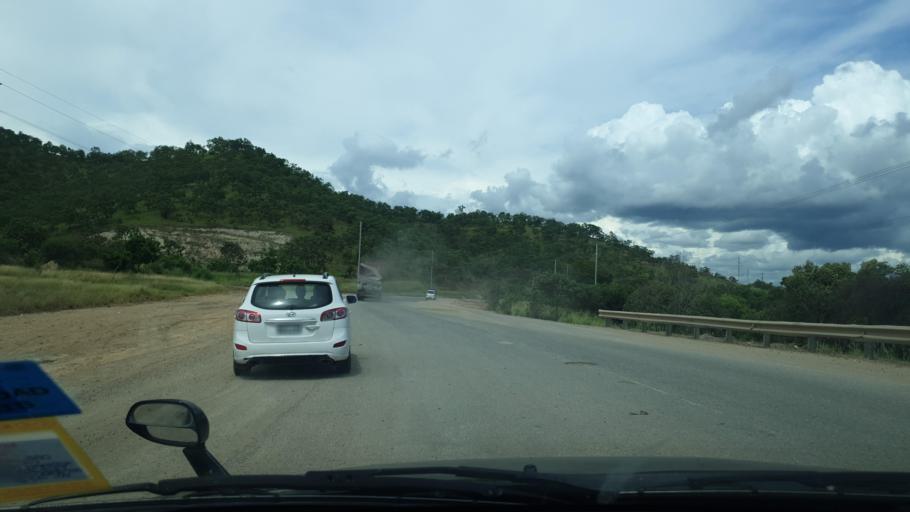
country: PG
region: National Capital
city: Port Moresby
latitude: -9.4200
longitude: 147.0930
